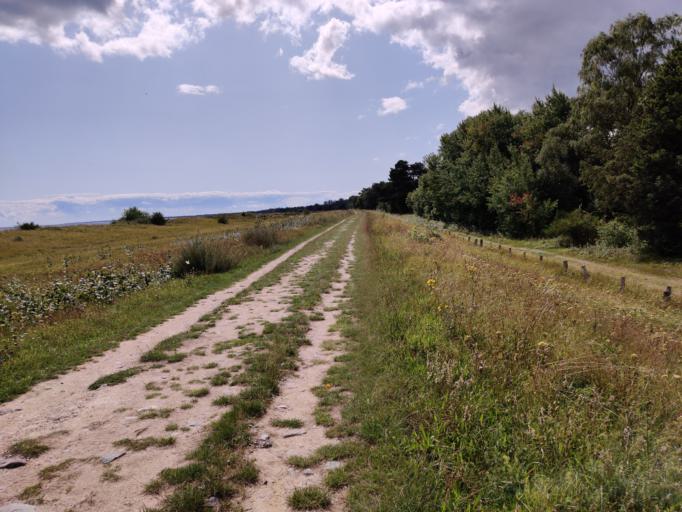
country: DK
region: Zealand
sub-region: Guldborgsund Kommune
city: Nykobing Falster
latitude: 54.7021
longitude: 11.9783
